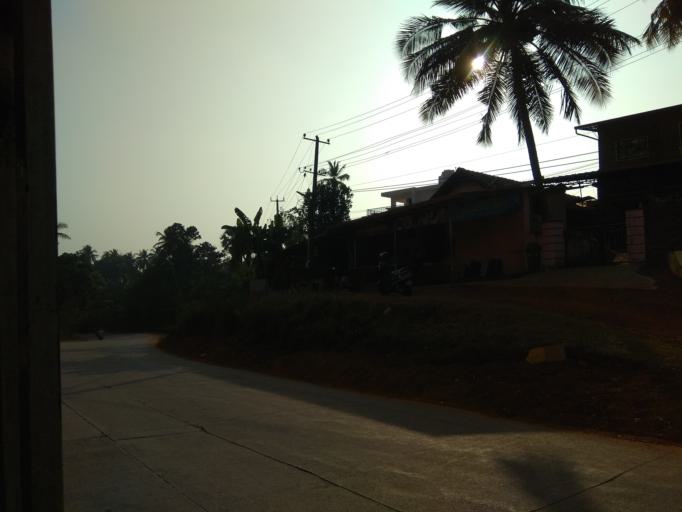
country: IN
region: Karnataka
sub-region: Dakshina Kannada
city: Mangalore
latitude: 12.9208
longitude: 74.8595
